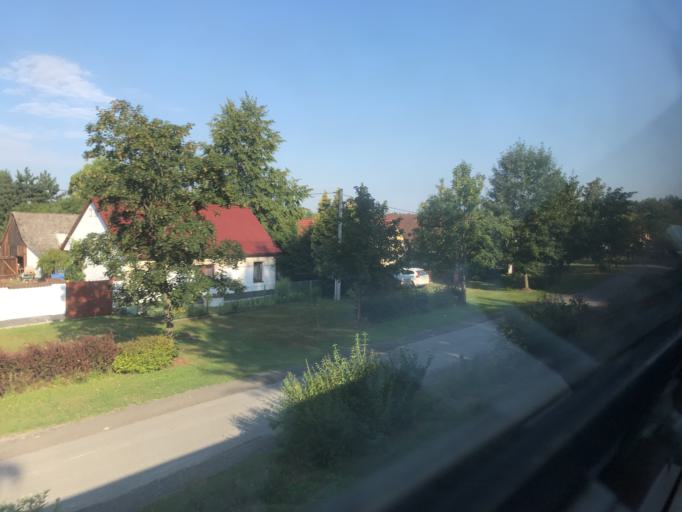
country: CZ
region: Jihocesky
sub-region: Okres Tabor
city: Veseli nad Luznici
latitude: 49.1559
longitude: 14.7237
